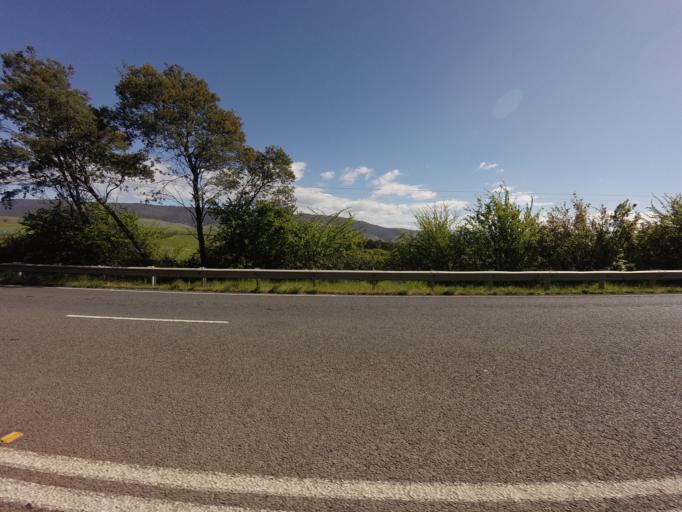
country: AU
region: Tasmania
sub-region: Derwent Valley
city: New Norfolk
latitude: -42.7169
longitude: 146.9477
